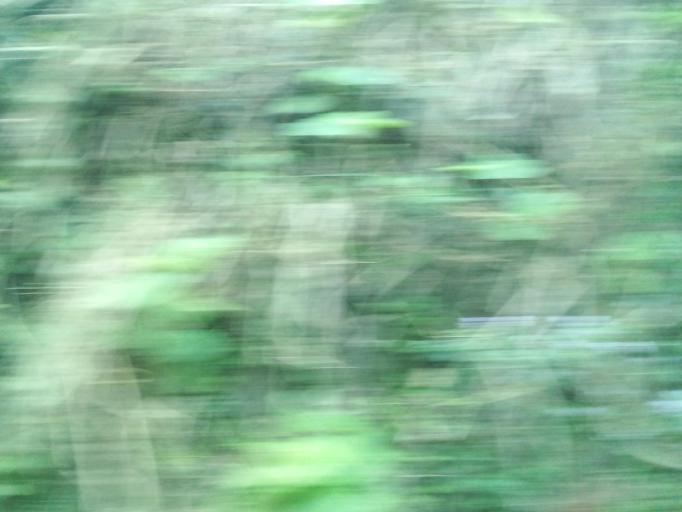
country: BR
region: Minas Gerais
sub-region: Joao Monlevade
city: Joao Monlevade
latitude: -19.8265
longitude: -43.1113
